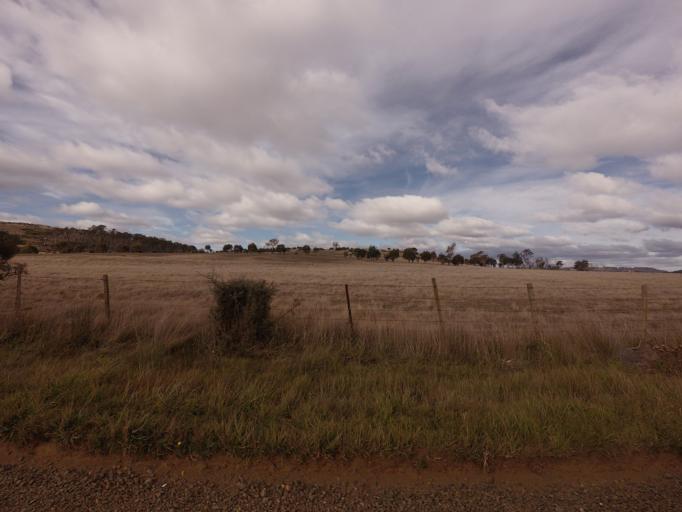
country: AU
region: Tasmania
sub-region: Brighton
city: Bridgewater
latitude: -42.4218
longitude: 147.3917
